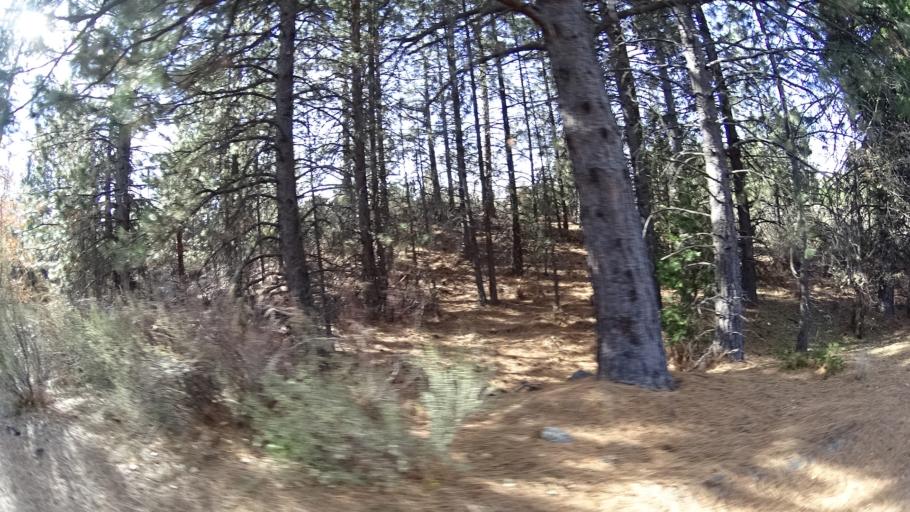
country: US
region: California
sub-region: Siskiyou County
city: Weed
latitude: 41.4254
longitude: -122.3963
